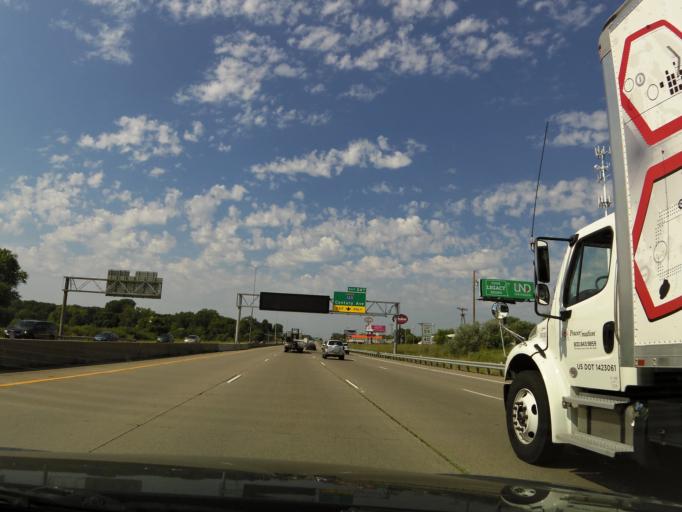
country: US
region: Minnesota
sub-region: Washington County
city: Oakdale
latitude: 44.9486
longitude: -92.9719
